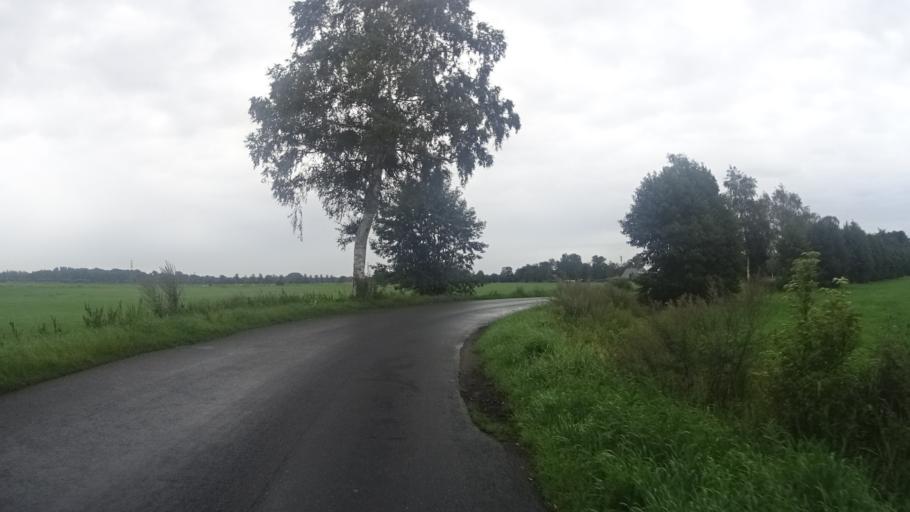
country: DE
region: Schleswig-Holstein
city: Raa-Besenbek
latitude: 53.7891
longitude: 9.5931
